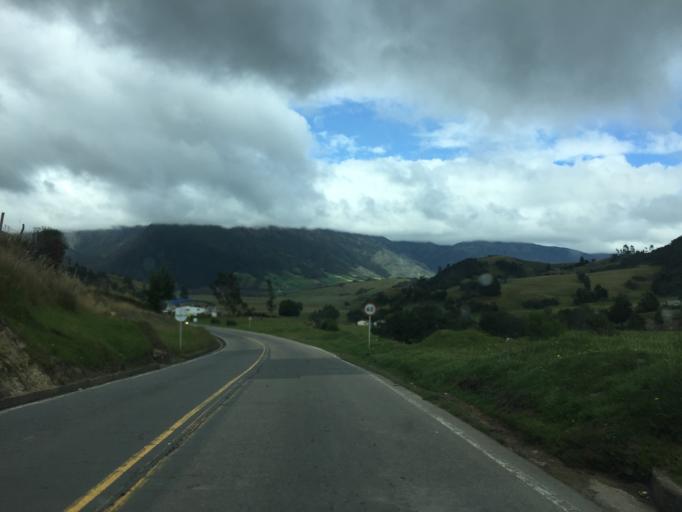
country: CO
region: Boyaca
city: Combita
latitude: 5.6881
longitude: -73.3667
